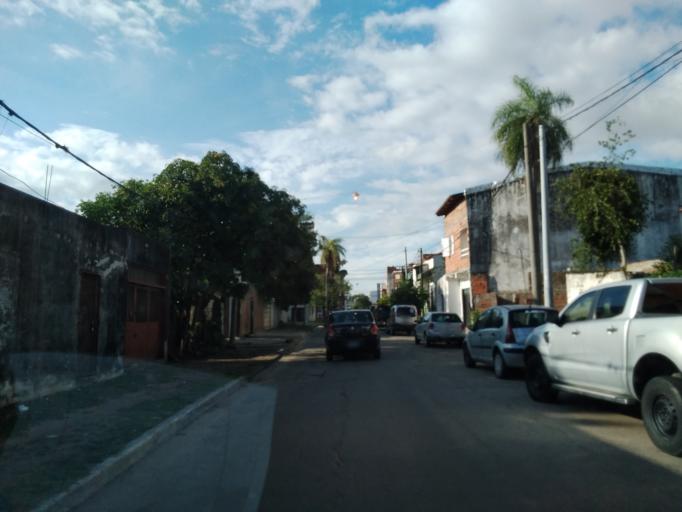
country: AR
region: Corrientes
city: Corrientes
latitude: -27.4661
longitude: -58.8221
